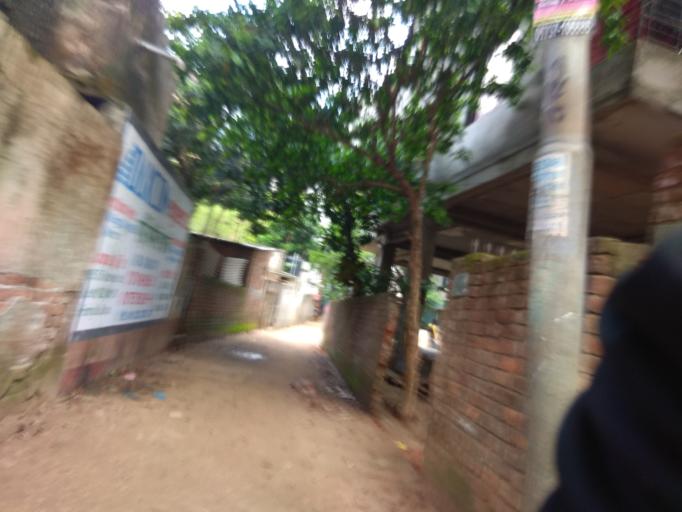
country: BD
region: Dhaka
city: Tungi
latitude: 23.8247
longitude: 90.3877
